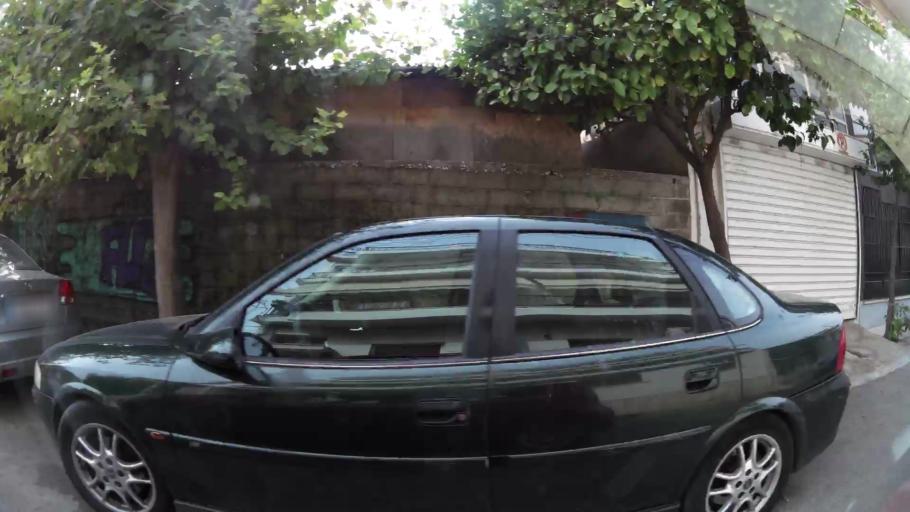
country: GR
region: Attica
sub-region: Nomarchia Athinas
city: Peristeri
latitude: 38.0101
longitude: 23.6816
